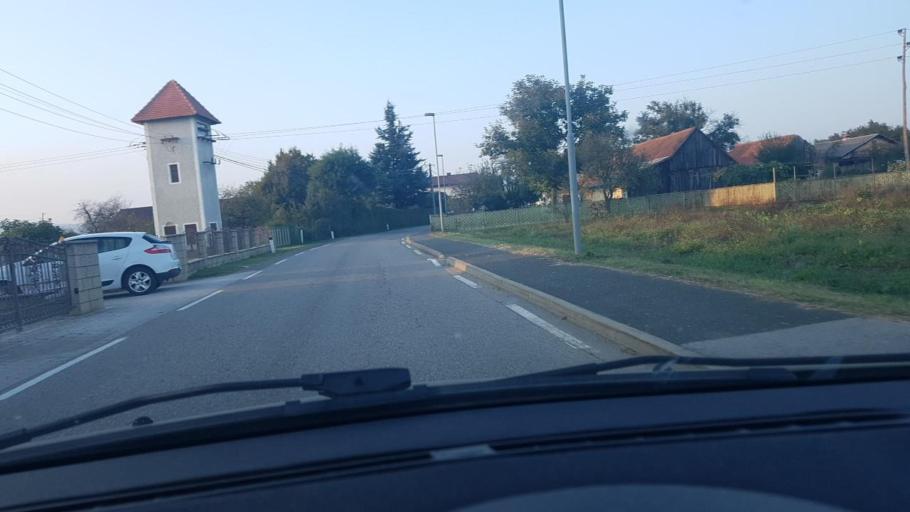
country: SI
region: Race-Fram
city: Race
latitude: 46.4311
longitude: 15.6980
